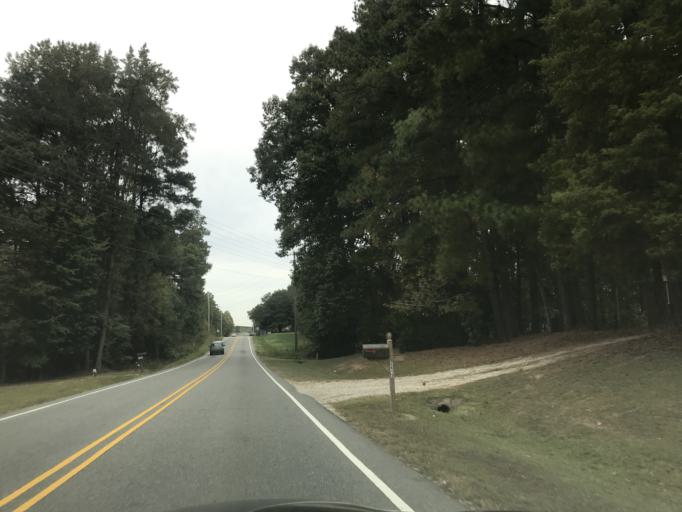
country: US
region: North Carolina
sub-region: Wake County
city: Rolesville
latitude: 35.9070
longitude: -78.5050
